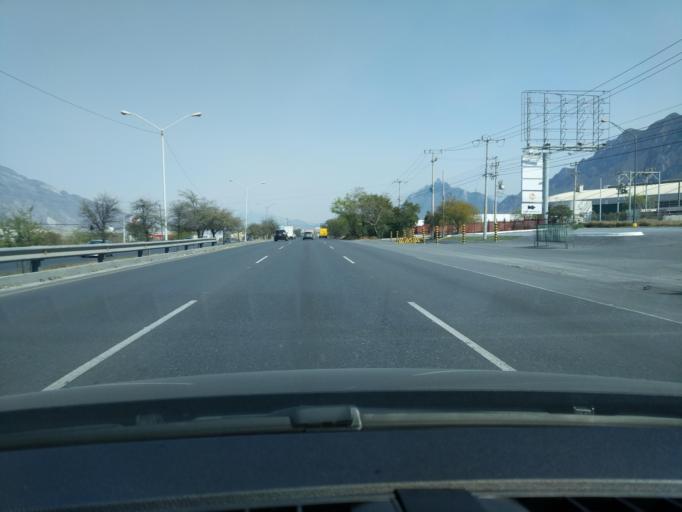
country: MX
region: Nuevo Leon
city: Santa Catarina
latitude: 25.6909
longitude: -100.5046
